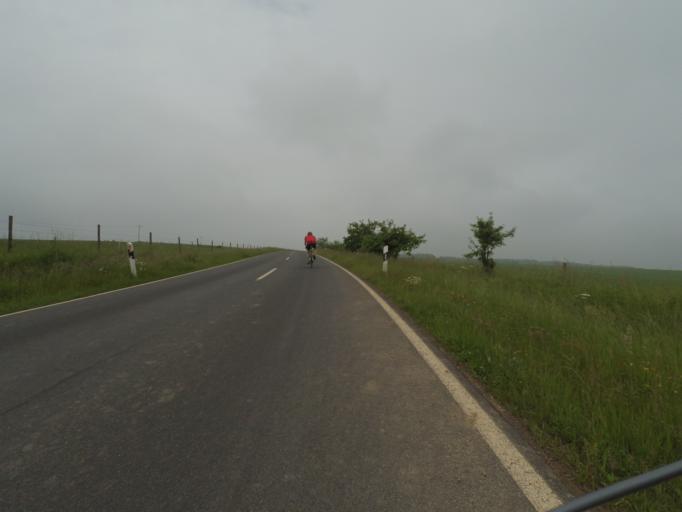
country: DE
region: Rheinland-Pfalz
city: Ernst
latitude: 50.1498
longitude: 7.2553
